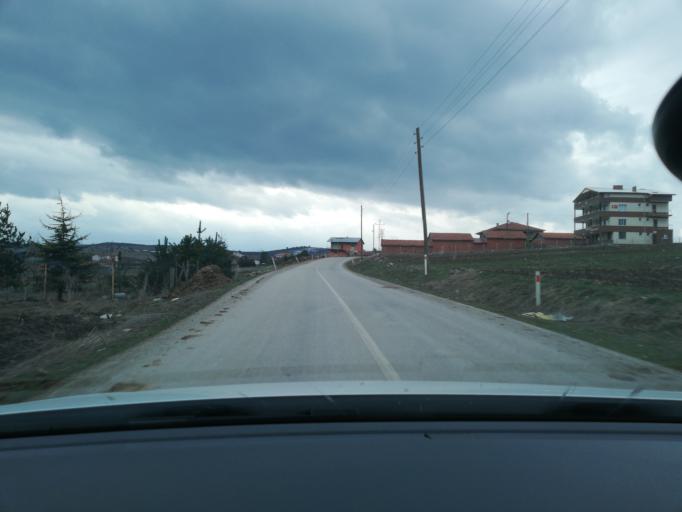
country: TR
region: Bolu
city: Gerede
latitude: 40.6922
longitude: 32.2159
